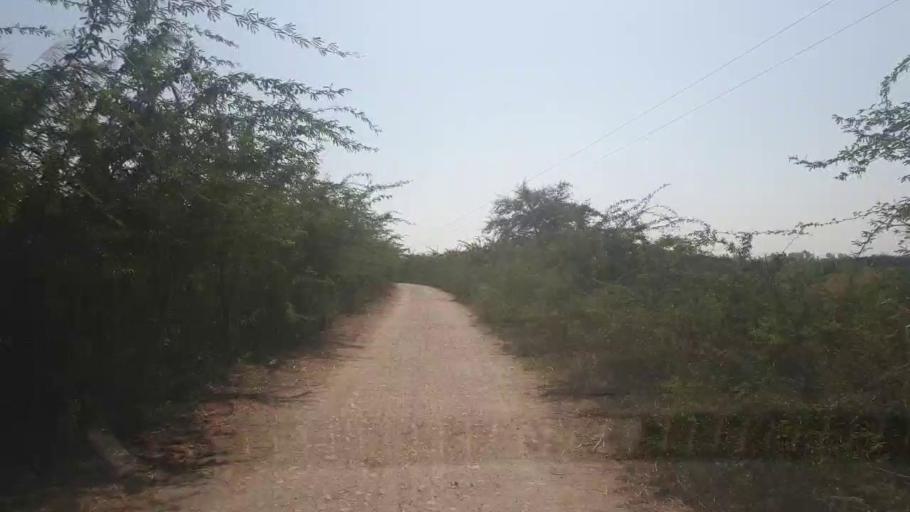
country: PK
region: Sindh
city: Badin
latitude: 24.6360
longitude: 68.9120
